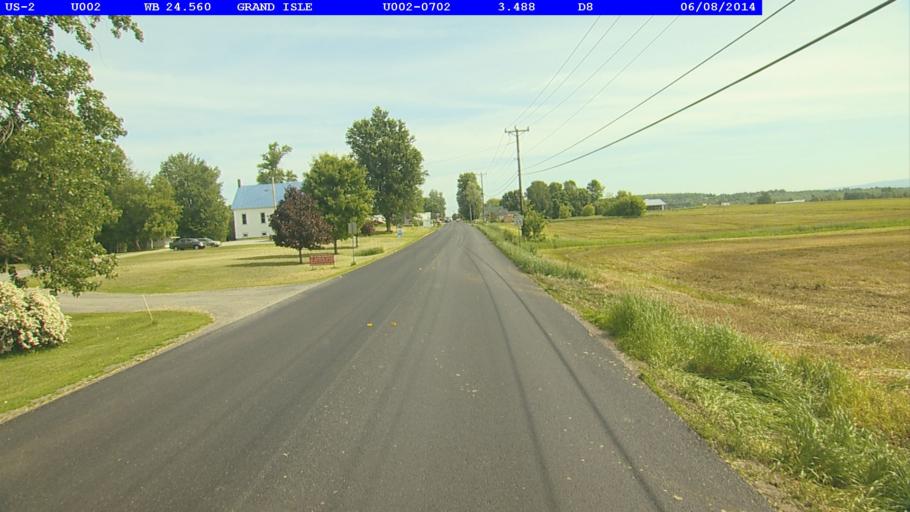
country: US
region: Vermont
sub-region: Grand Isle County
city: North Hero
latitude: 44.7177
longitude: -73.2960
